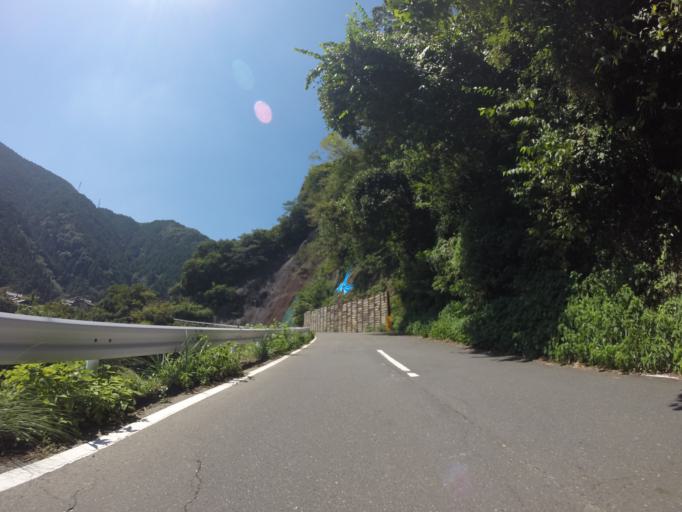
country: JP
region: Shizuoka
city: Shizuoka-shi
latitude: 35.0500
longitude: 138.2440
